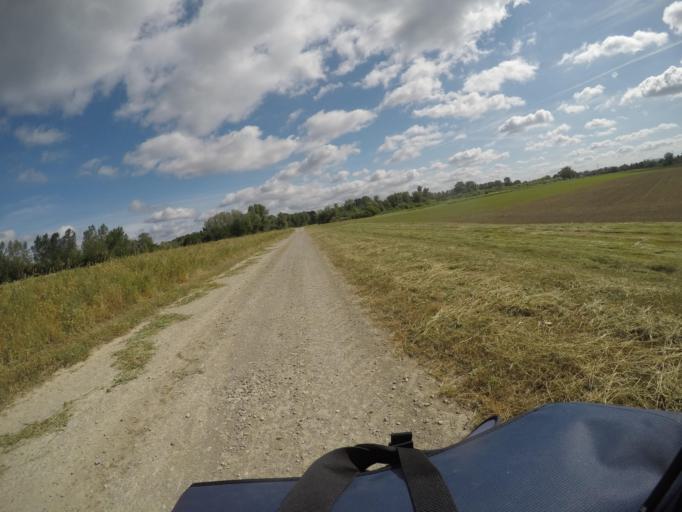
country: DE
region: Baden-Wuerttemberg
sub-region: Karlsruhe Region
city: Au am Rhein
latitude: 48.9396
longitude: 8.2002
